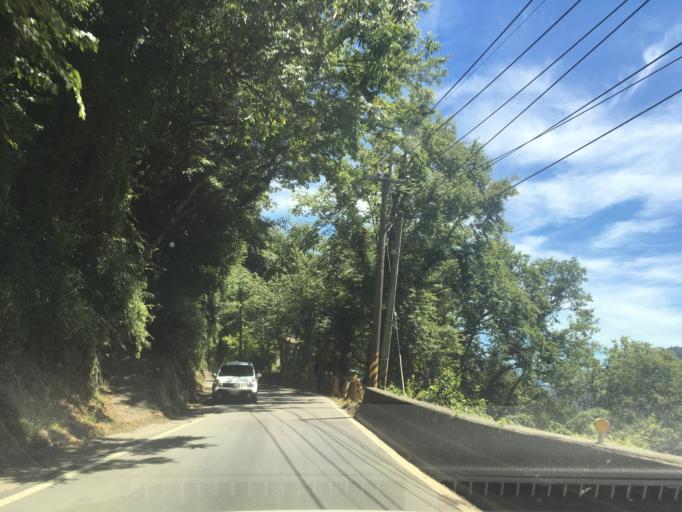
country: TW
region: Taiwan
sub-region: Nantou
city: Puli
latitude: 24.2308
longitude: 121.2533
